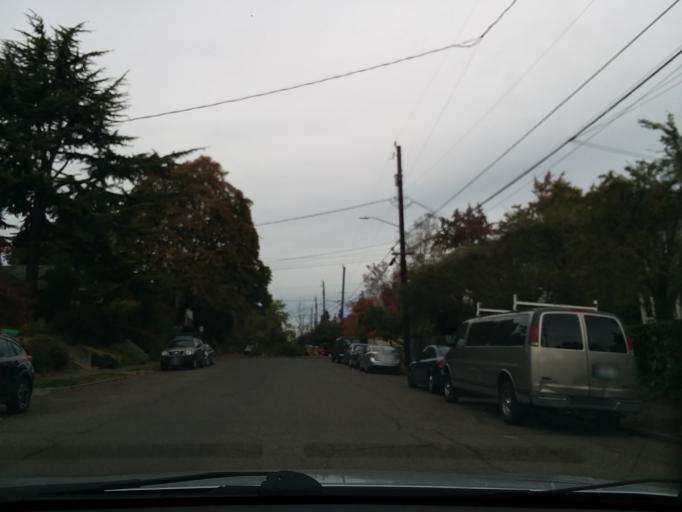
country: US
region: Washington
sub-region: King County
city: Seattle
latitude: 47.6561
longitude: -122.3447
